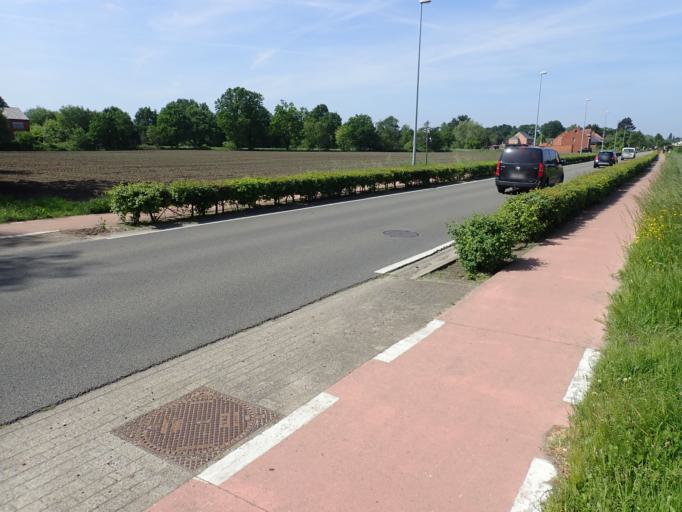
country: BE
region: Flanders
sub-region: Provincie Antwerpen
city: Herselt
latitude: 51.0877
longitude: 4.8550
